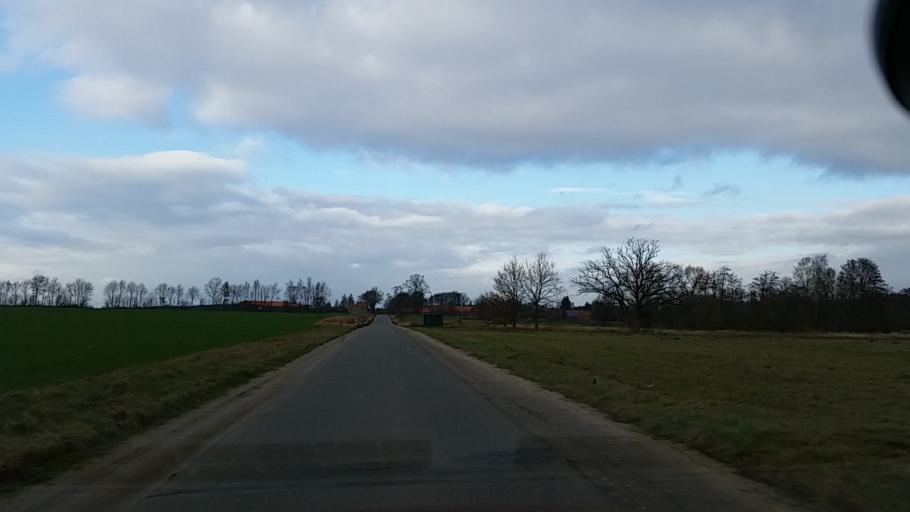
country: DE
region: Lower Saxony
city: Wieren
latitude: 52.8760
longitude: 10.6565
